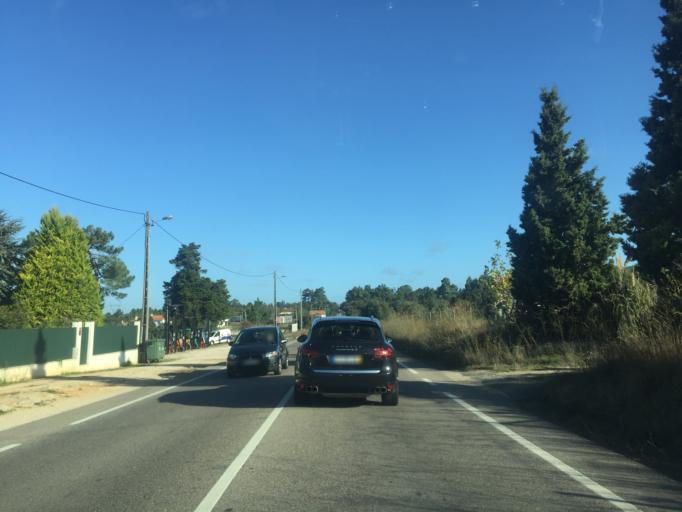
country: PT
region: Leiria
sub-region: Alcobaca
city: Benedita
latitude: 39.3851
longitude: -8.9611
